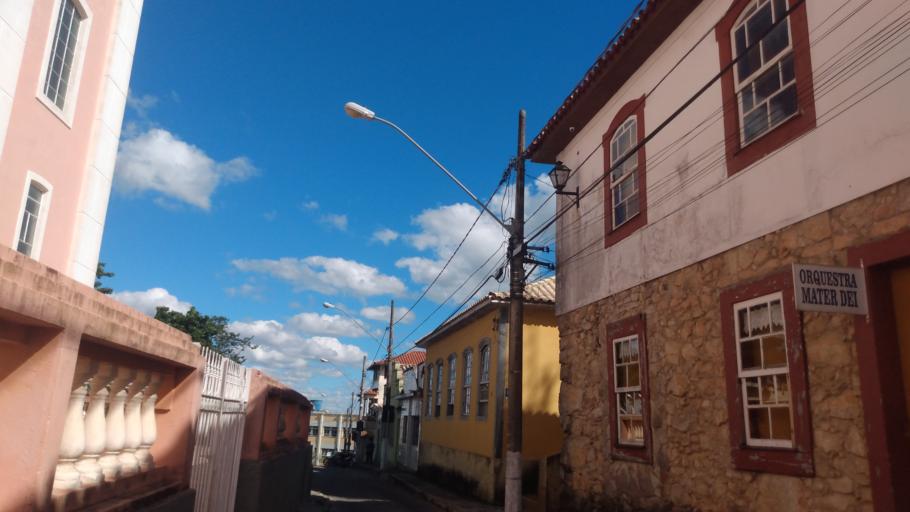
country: BR
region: Minas Gerais
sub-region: Tiradentes
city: Tiradentes
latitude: -20.9228
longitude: -44.2381
